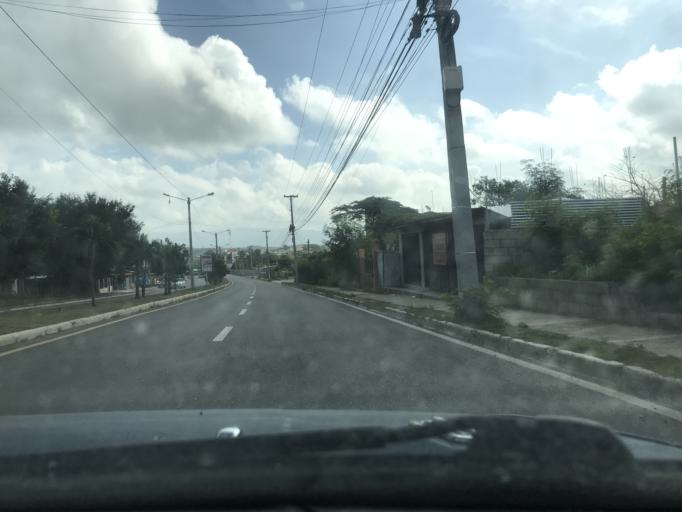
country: DO
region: Santiago
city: Santiago de los Caballeros
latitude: 19.4299
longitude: -70.7265
